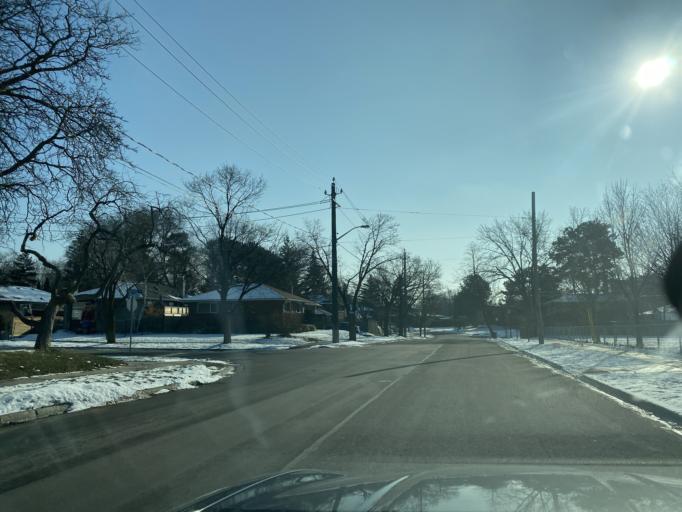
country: CA
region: Ontario
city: Etobicoke
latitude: 43.6596
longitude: -79.5646
